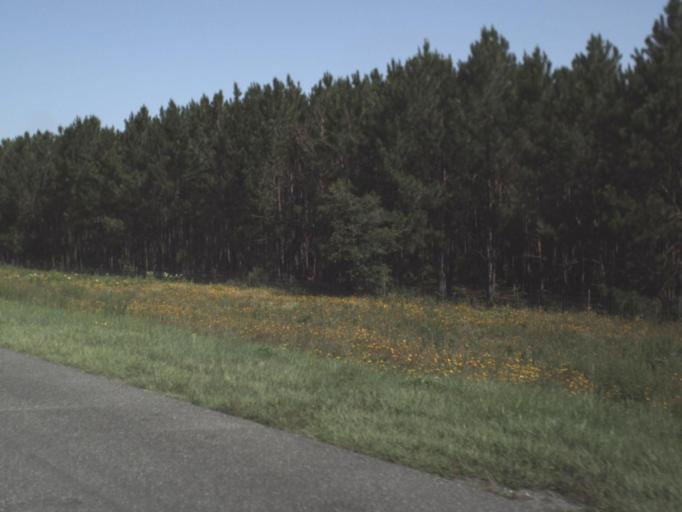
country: US
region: Florida
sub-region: Suwannee County
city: Wellborn
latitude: 30.2886
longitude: -82.8568
